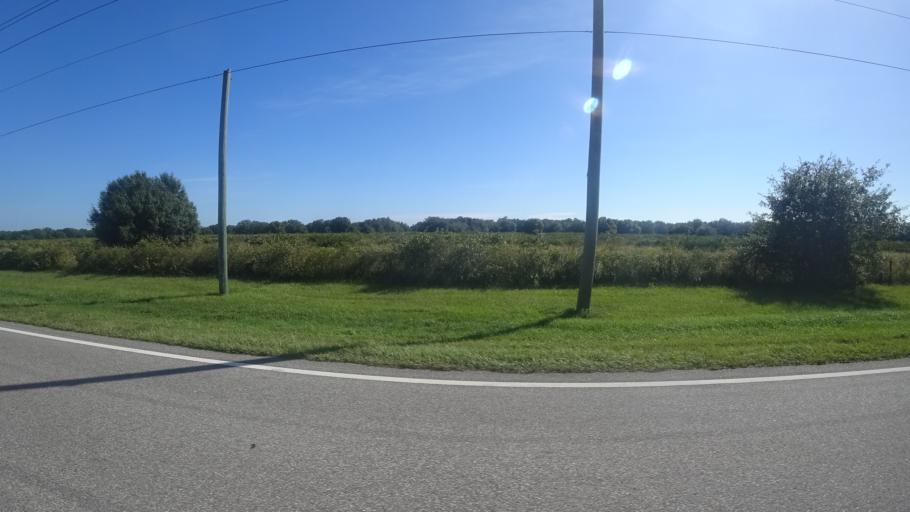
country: US
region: Florida
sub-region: Sarasota County
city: Lake Sarasota
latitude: 27.3736
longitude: -82.2683
